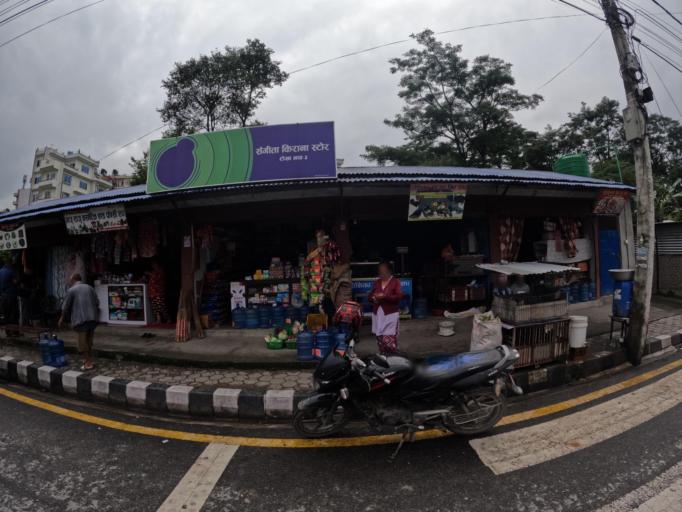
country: NP
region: Central Region
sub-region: Bagmati Zone
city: Kathmandu
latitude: 27.7588
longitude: 85.3261
